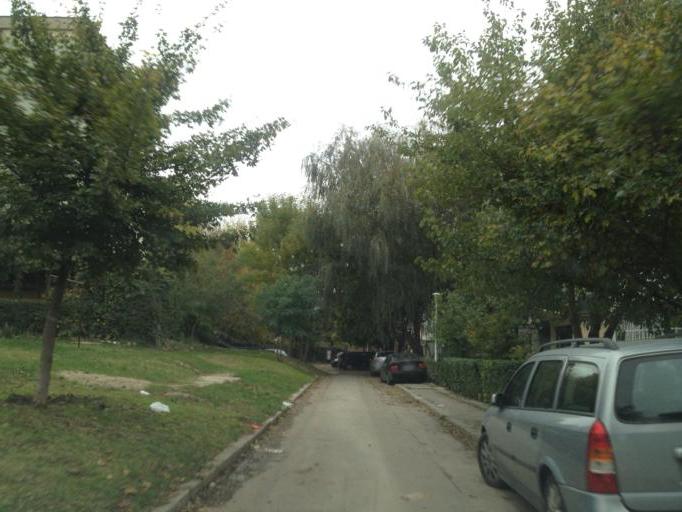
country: RO
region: Dolj
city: Craiova
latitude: 44.3267
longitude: 23.7877
